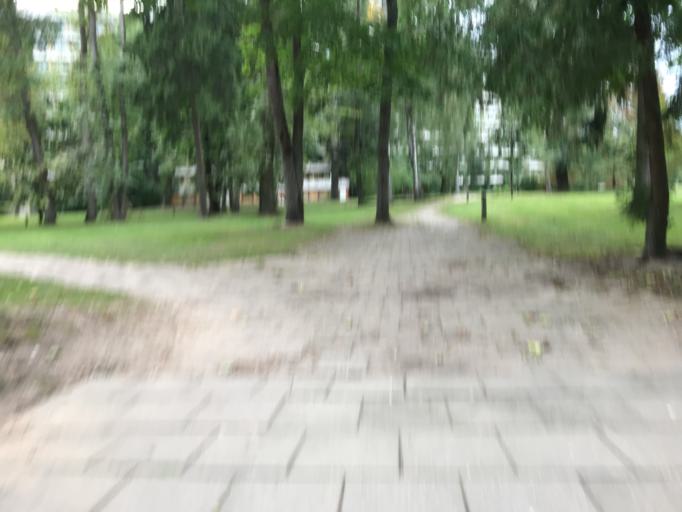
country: LT
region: Alytaus apskritis
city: Druskininkai
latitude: 54.0214
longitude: 23.9706
